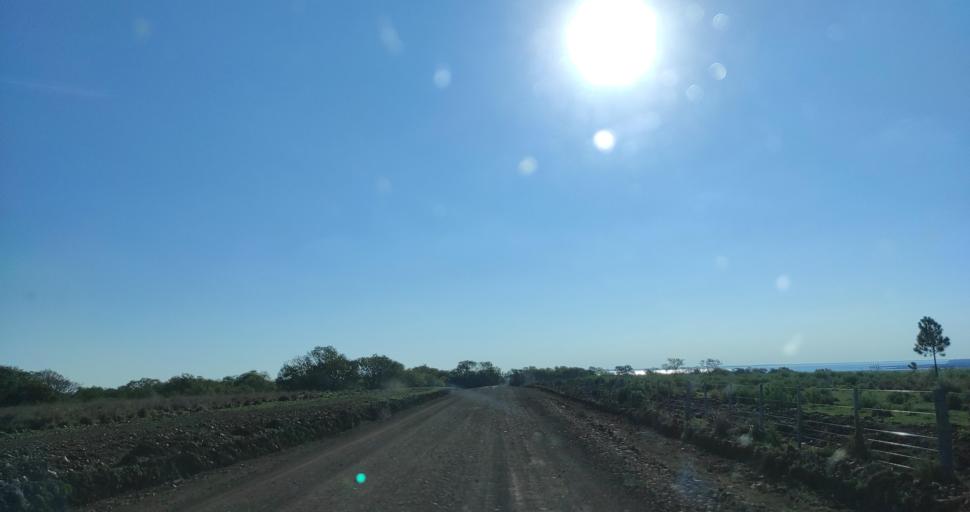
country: PY
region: Itapua
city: San Juan del Parana
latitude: -27.4211
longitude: -56.1184
